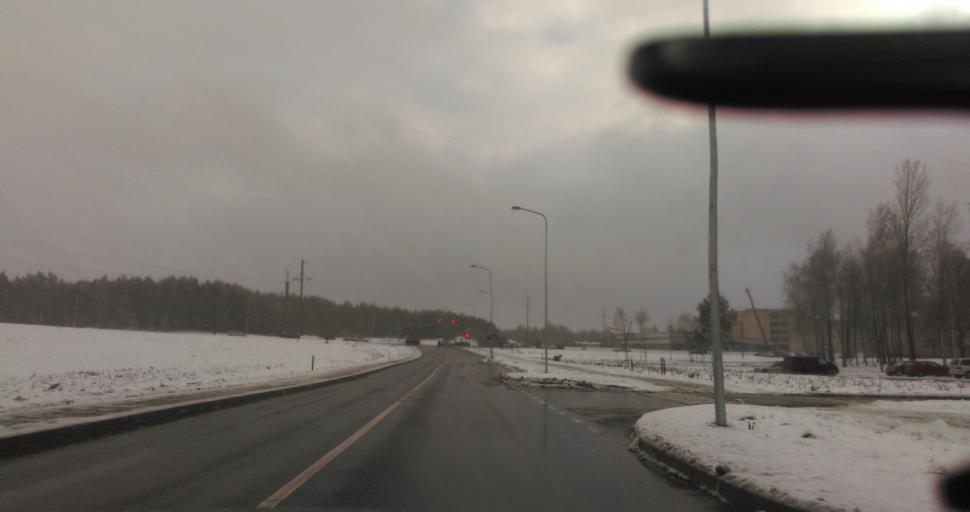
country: LT
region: Utenos apskritis
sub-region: Utena
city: Utena
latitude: 55.5050
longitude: 25.6176
